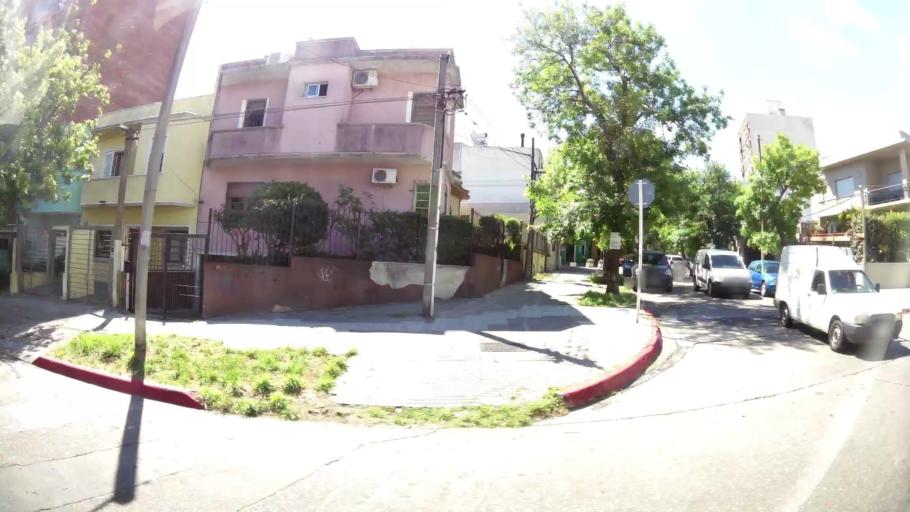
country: UY
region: Montevideo
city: Montevideo
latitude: -34.9043
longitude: -56.1447
